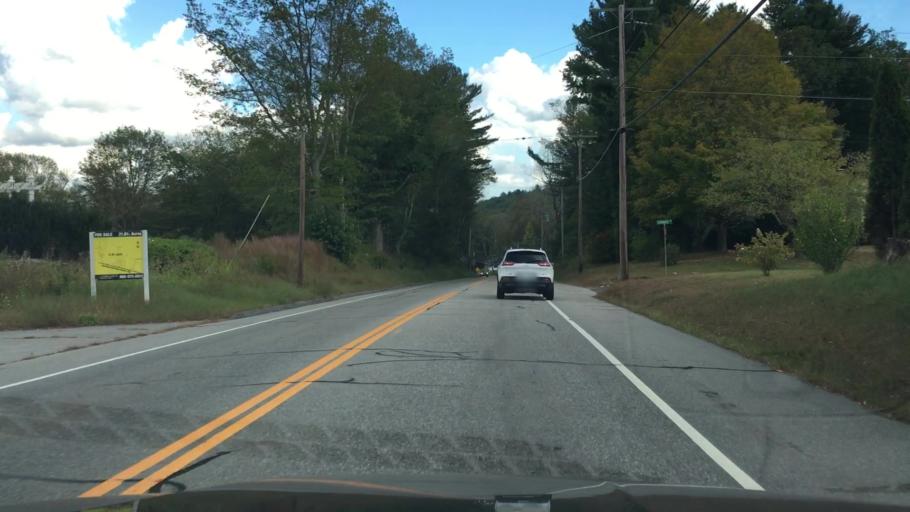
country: US
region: Connecticut
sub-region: Tolland County
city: Crystal Lake
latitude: 41.9730
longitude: -72.3679
